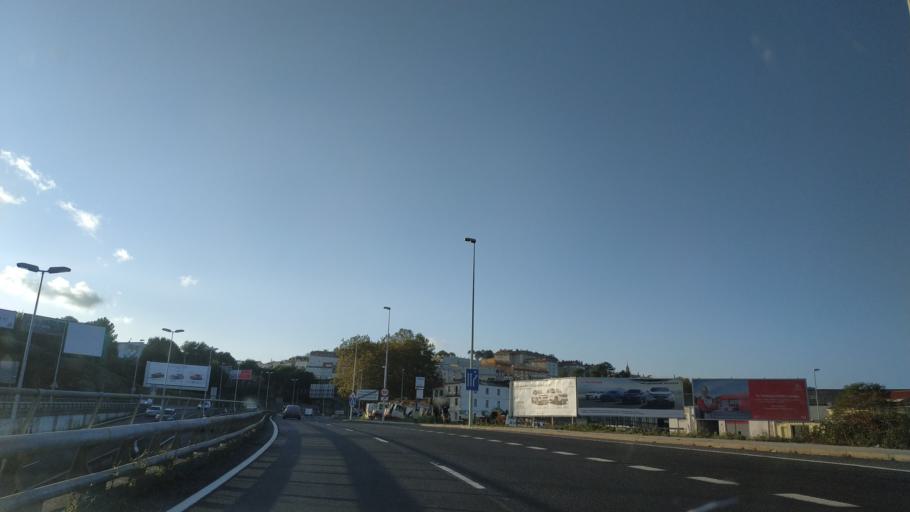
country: ES
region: Galicia
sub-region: Provincia da Coruna
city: A Coruna
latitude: 43.3324
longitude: -8.3863
